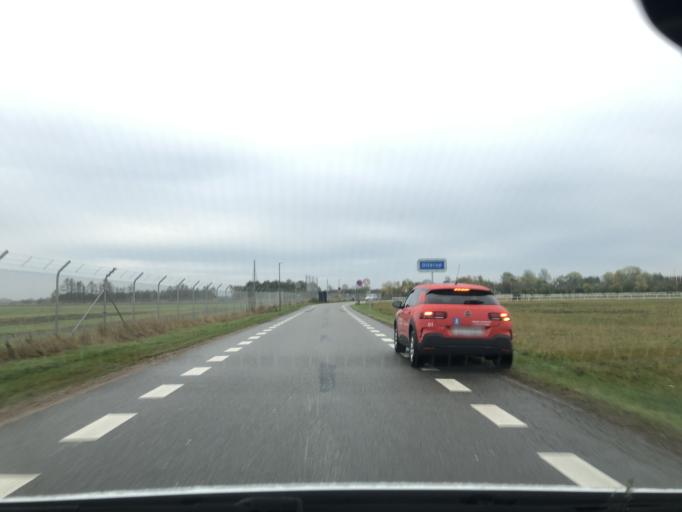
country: DK
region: Capital Region
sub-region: Tarnby Kommune
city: Tarnby
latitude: 55.5877
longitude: 12.5983
